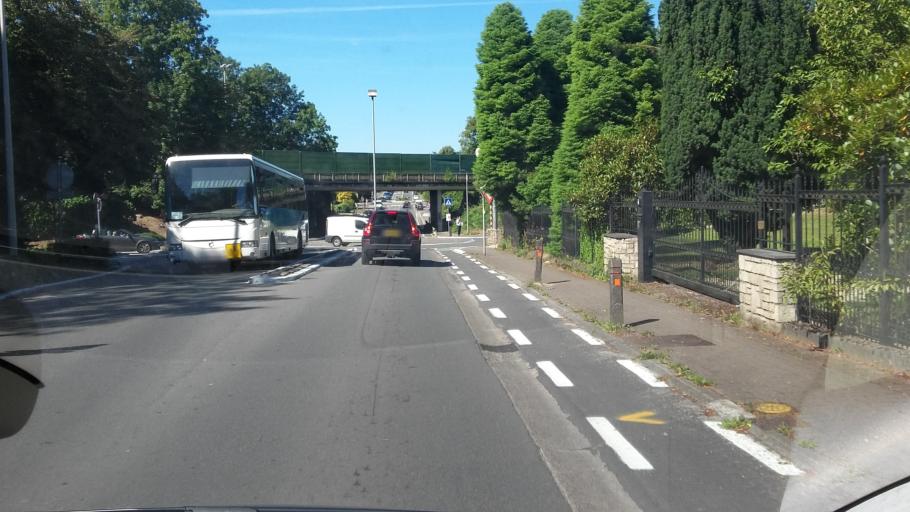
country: BE
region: Wallonia
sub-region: Province du Brabant Wallon
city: Waterloo
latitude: 50.7059
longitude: 4.4139
